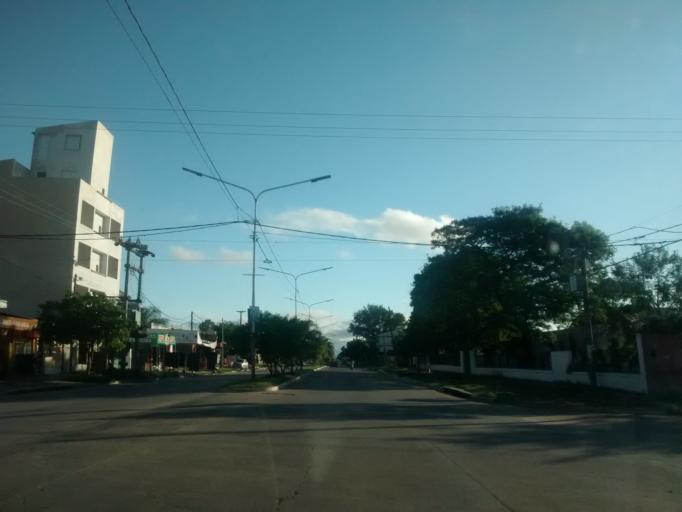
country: AR
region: Chaco
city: Resistencia
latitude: -27.4679
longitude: -59.0052
